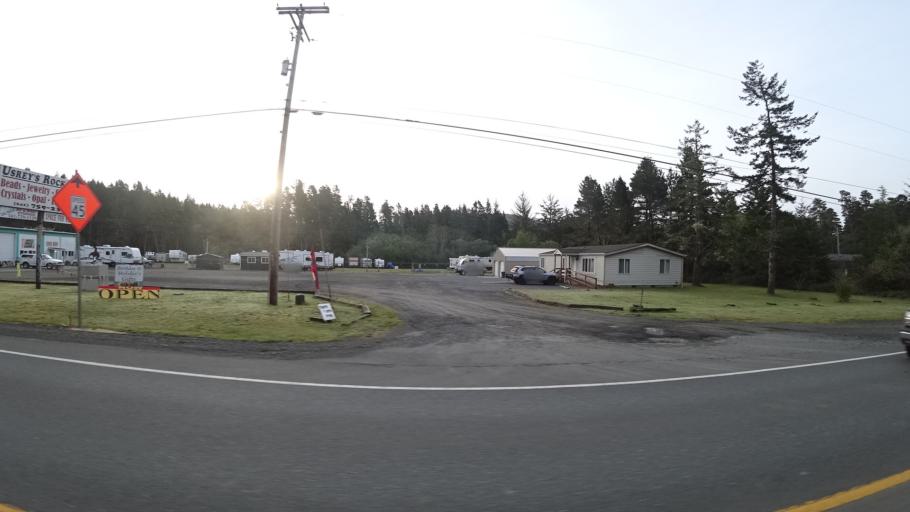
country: US
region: Oregon
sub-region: Coos County
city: Lakeside
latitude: 43.5977
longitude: -124.1806
